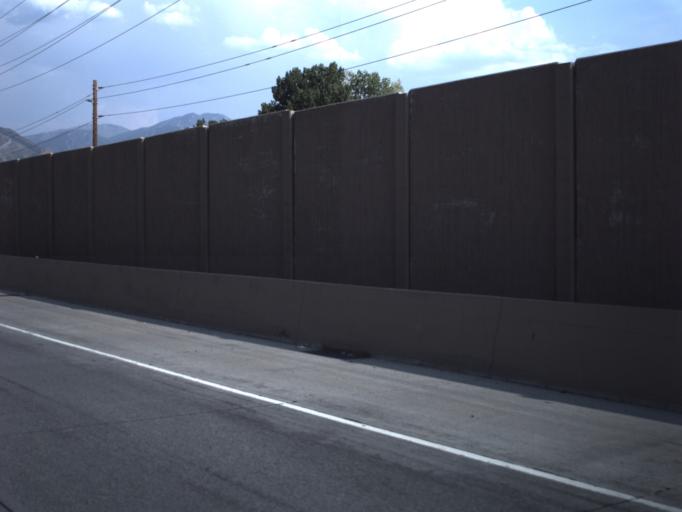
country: US
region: Utah
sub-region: Salt Lake County
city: South Salt Lake
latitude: 40.7193
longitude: -111.8644
